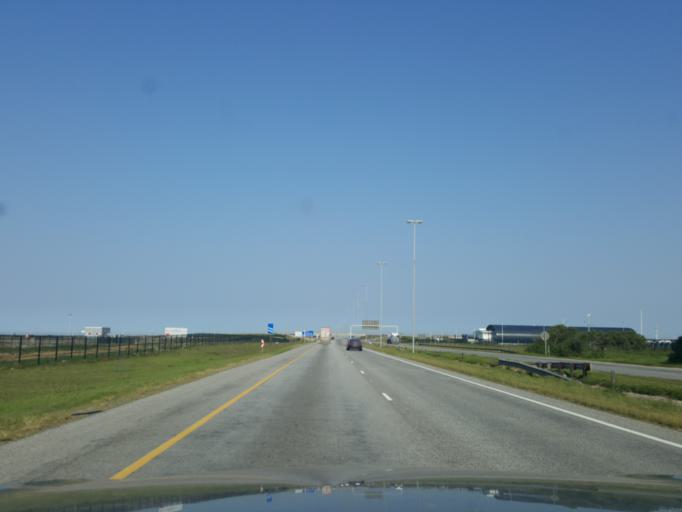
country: ZA
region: Eastern Cape
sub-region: Nelson Mandela Bay Metropolitan Municipality
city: Port Elizabeth
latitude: -33.8159
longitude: 25.6501
